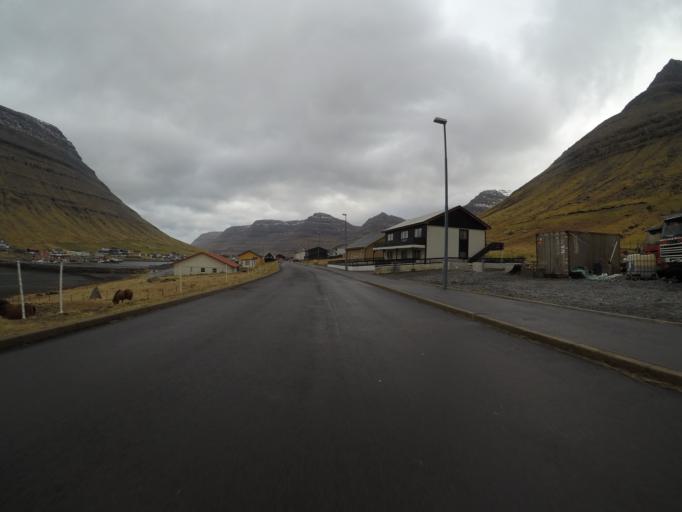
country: FO
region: Nordoyar
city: Klaksvik
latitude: 62.2999
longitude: -6.5308
